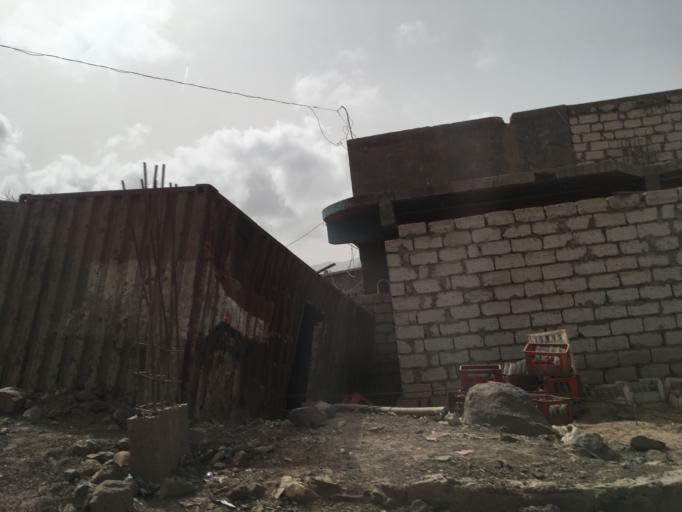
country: YE
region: Ad Dali'
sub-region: Ad Dhale'e
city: Dhalie
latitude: 13.7028
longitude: 44.7377
